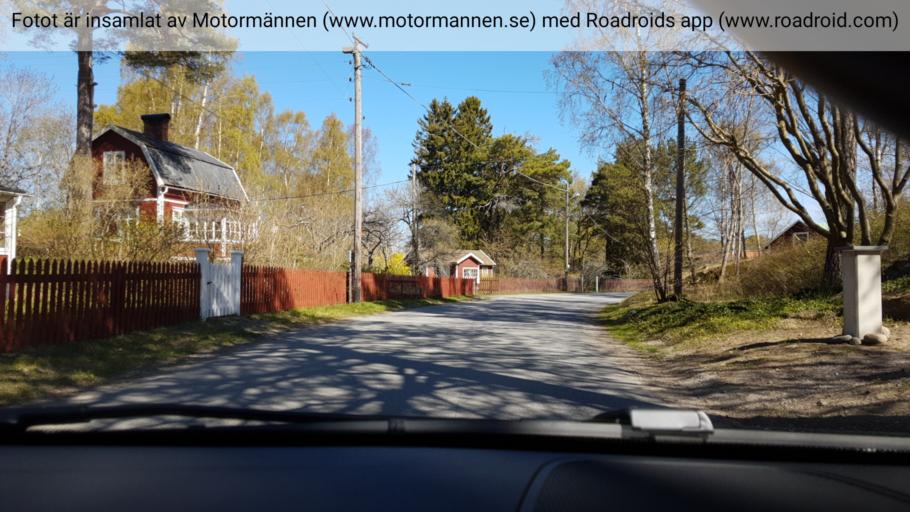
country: SE
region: Stockholm
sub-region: Varmdo Kommun
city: Holo
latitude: 59.2892
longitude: 18.6876
